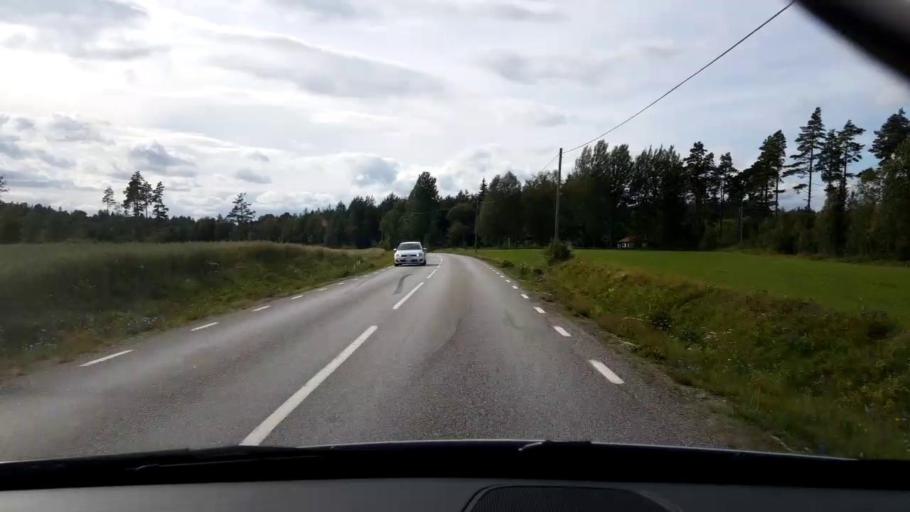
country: SE
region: Joenkoeping
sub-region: Vetlanda Kommun
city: Landsbro
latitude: 57.3800
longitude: 14.9869
